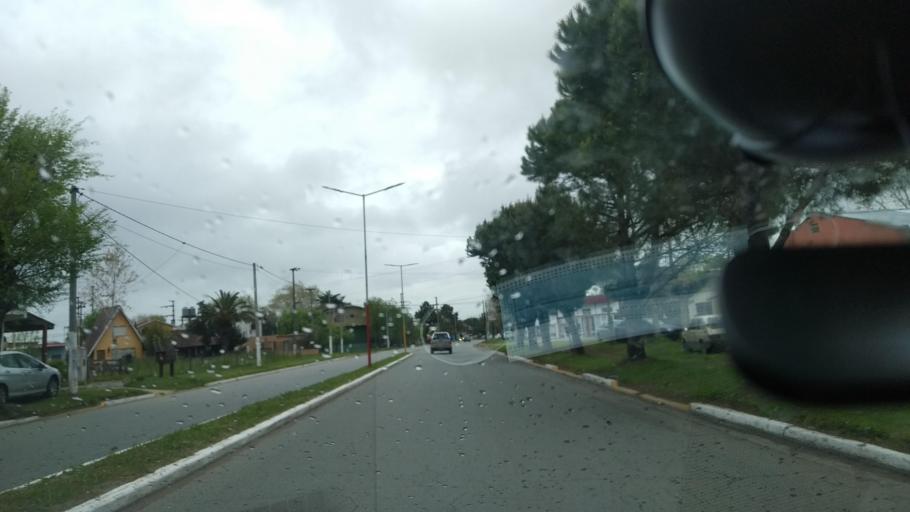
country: AR
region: Buenos Aires
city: San Clemente del Tuyu
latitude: -36.3794
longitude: -56.7210
